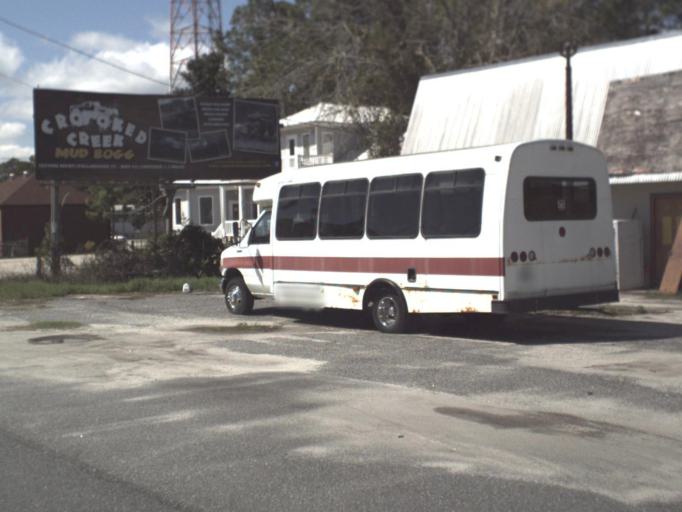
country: US
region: Florida
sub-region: Franklin County
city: Carrabelle
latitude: 29.8502
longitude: -84.6609
